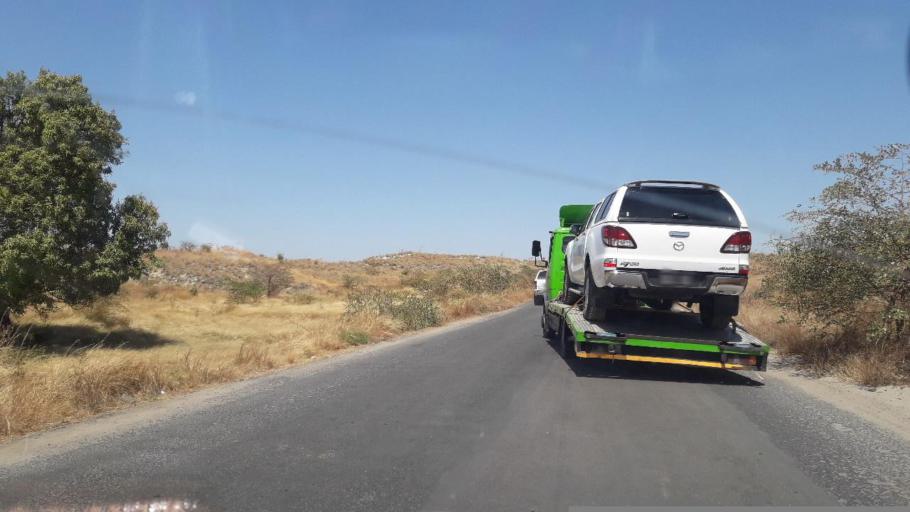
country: MG
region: Boeny
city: Ambato Boeny
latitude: -16.5231
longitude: 47.1371
